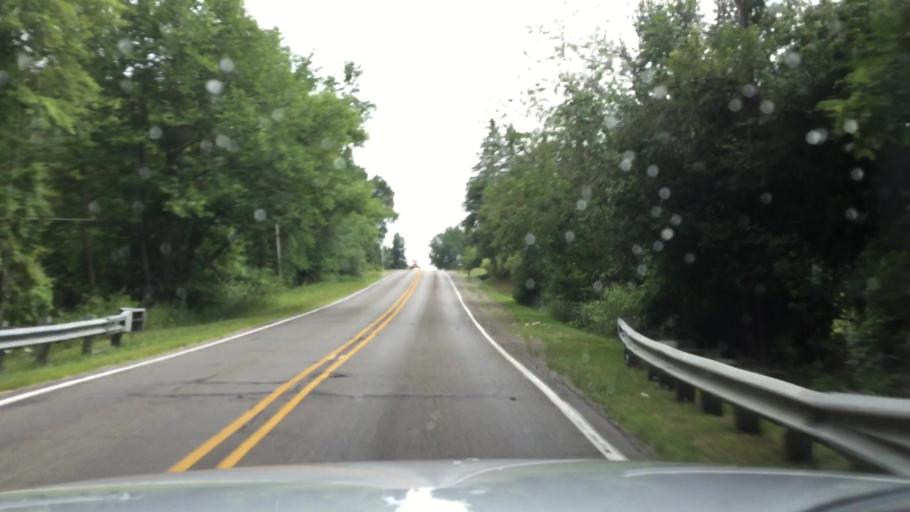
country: US
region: Michigan
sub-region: Genesee County
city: Clio
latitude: 43.1555
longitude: -83.7740
